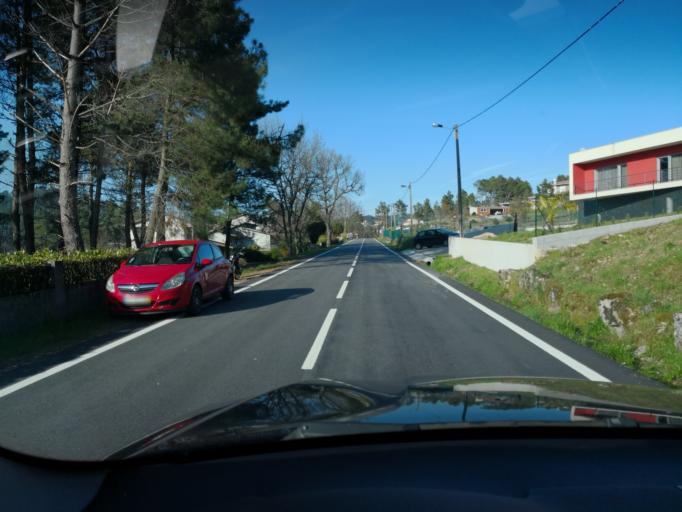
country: PT
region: Vila Real
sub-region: Vila Real
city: Vila Real
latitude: 41.3426
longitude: -7.6569
